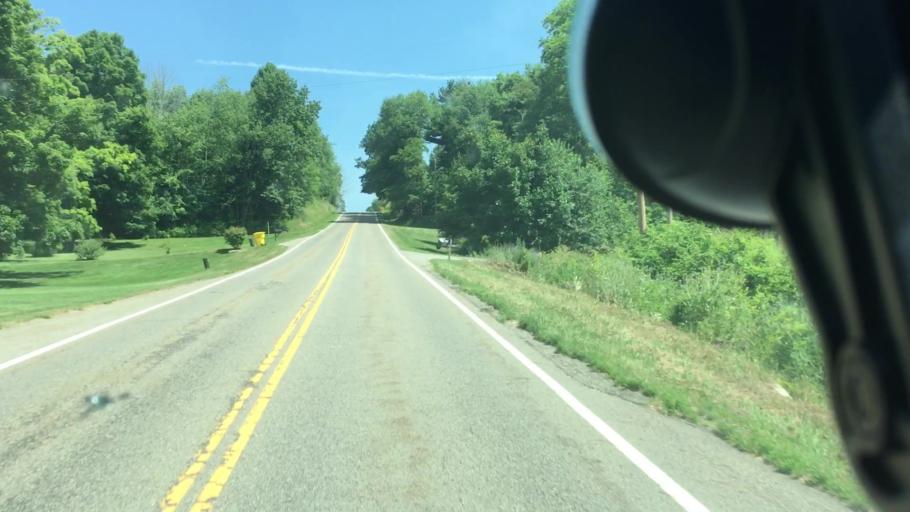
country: US
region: Ohio
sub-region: Columbiana County
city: Salem
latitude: 40.8235
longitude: -80.8581
